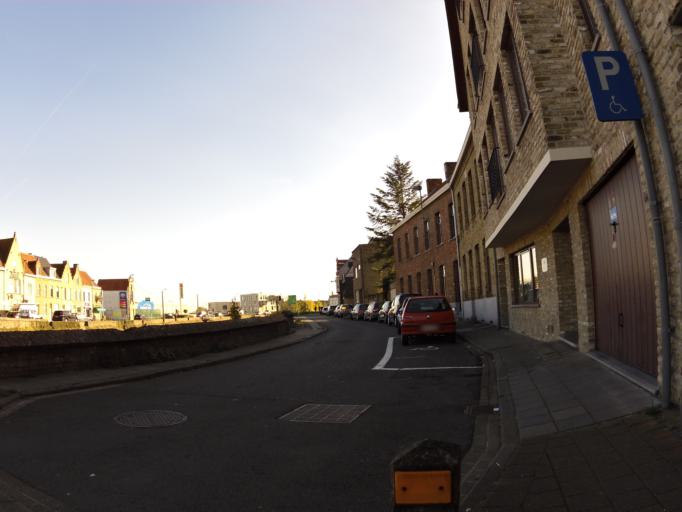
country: BE
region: Flanders
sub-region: Provincie West-Vlaanderen
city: Veurne
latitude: 51.0715
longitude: 2.6683
